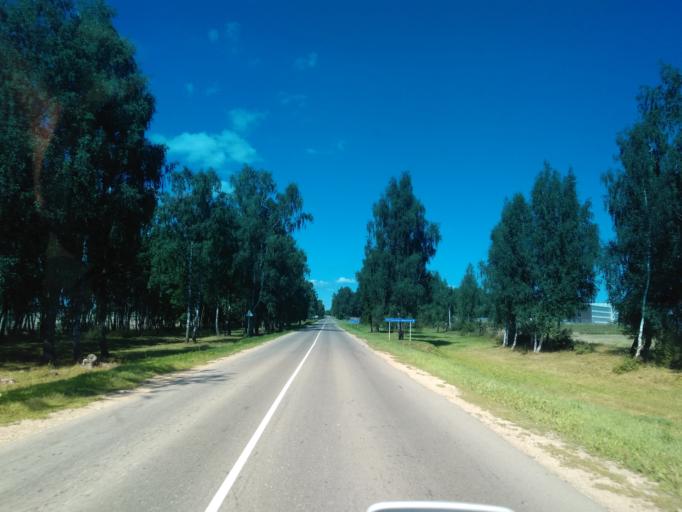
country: BY
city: Fanipol
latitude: 53.7220
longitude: 27.3388
